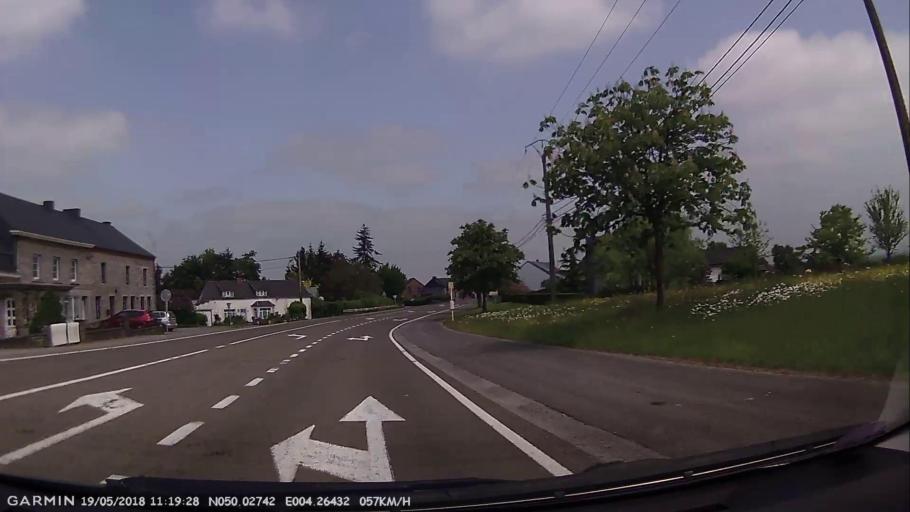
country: BE
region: Wallonia
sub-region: Province du Hainaut
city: Chimay
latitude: 50.0278
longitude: 4.2645
